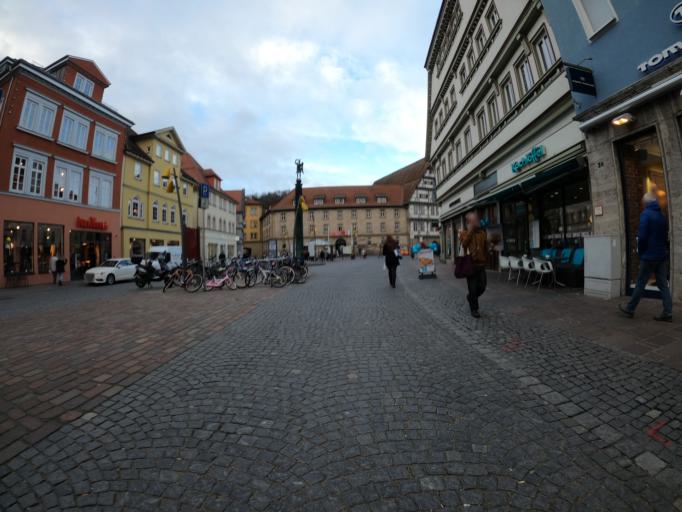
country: DE
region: Baden-Wuerttemberg
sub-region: Regierungsbezirk Stuttgart
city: Schwabisch Gmund
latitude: 48.8009
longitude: 9.7973
